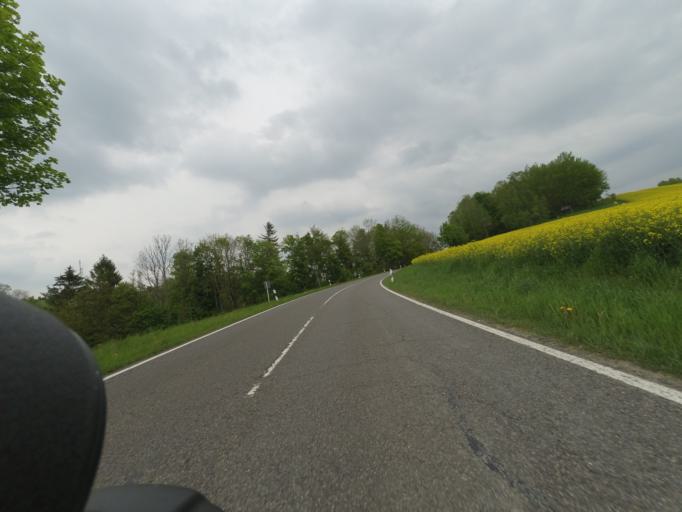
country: DE
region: Saxony
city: Pockau
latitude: 50.7105
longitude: 13.2341
